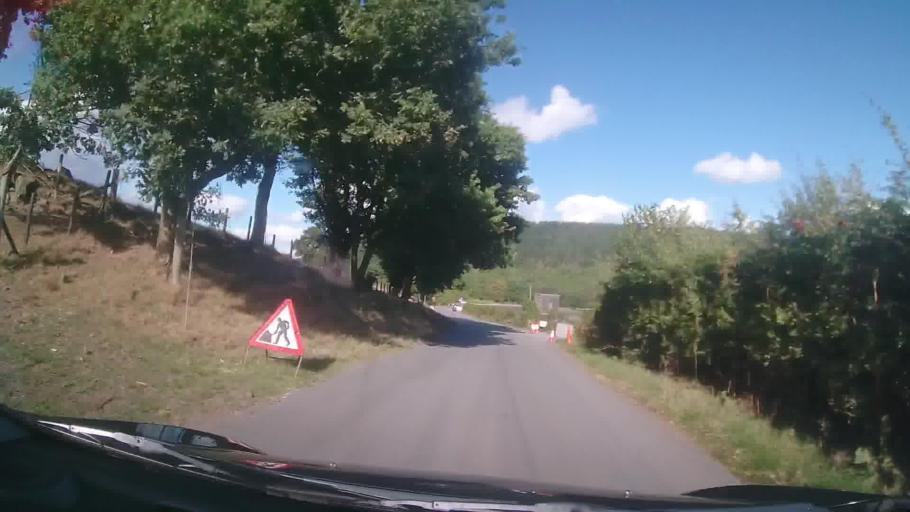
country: GB
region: Wales
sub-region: Sir Powys
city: Brecon
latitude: 51.8756
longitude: -3.3053
